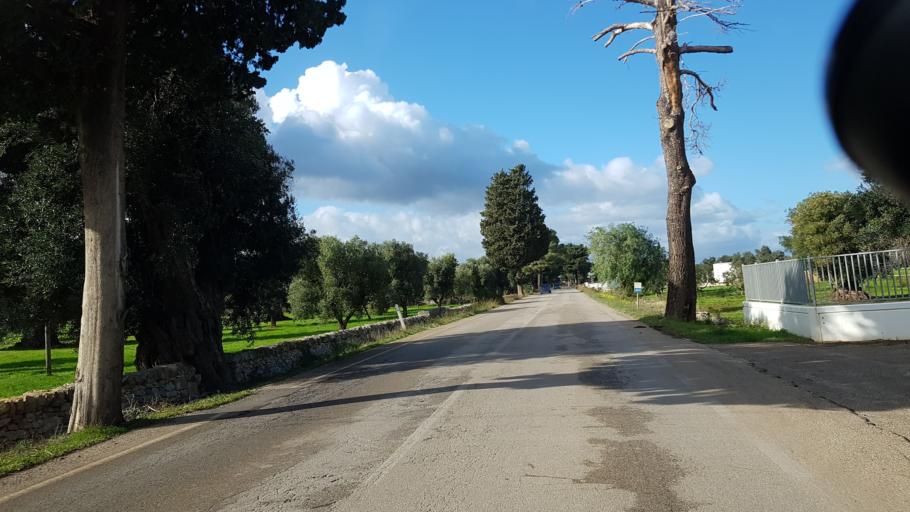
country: IT
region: Apulia
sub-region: Provincia di Brindisi
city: Montalbano
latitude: 40.7946
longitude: 17.4532
